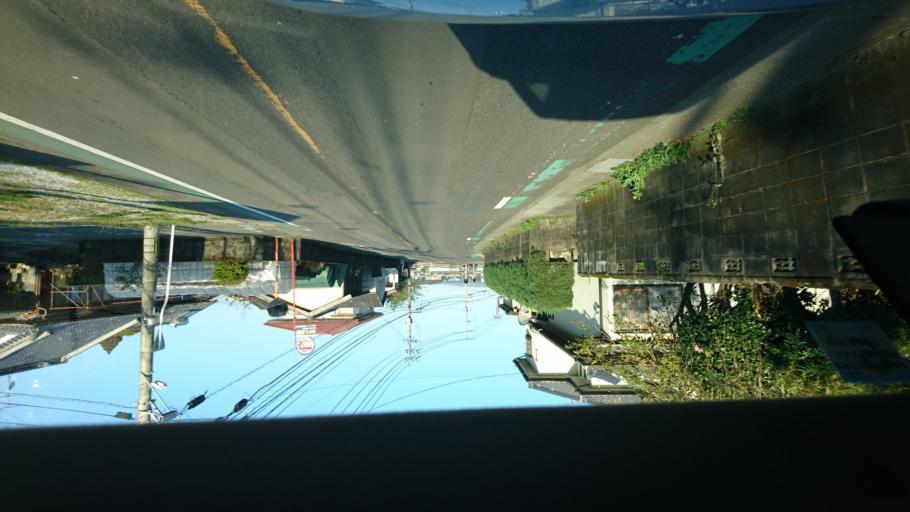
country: JP
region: Miyazaki
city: Miyazaki-shi
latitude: 31.8450
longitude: 131.3978
